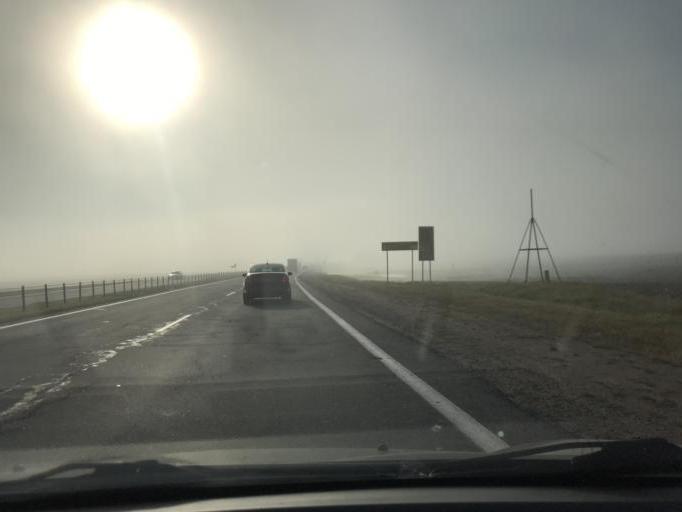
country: BY
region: Minsk
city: Dukora
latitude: 53.6753
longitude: 27.9308
